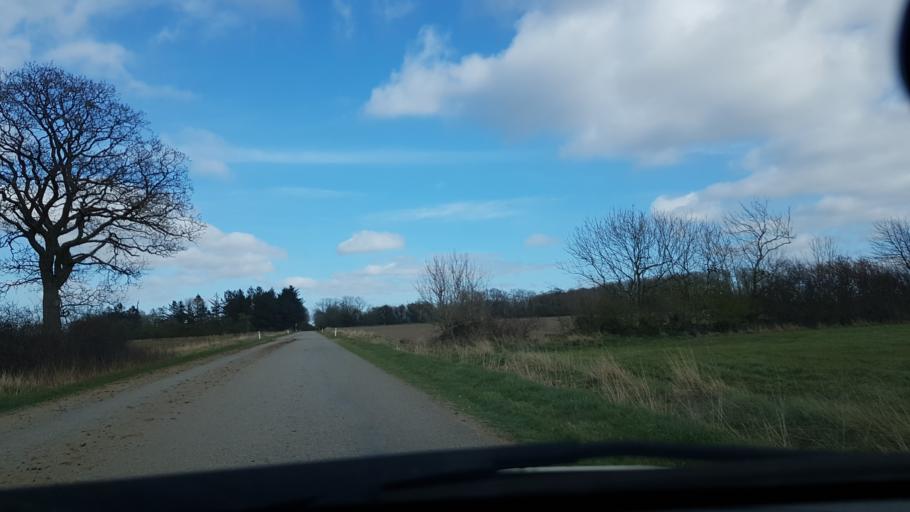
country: DK
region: South Denmark
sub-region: Vejen Kommune
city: Rodding
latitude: 55.4248
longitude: 9.0818
